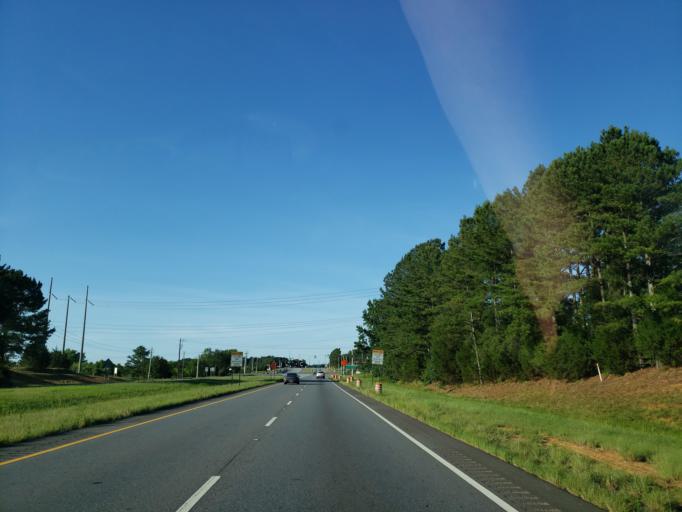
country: US
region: Georgia
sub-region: Floyd County
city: Shannon
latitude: 34.3631
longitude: -85.0531
